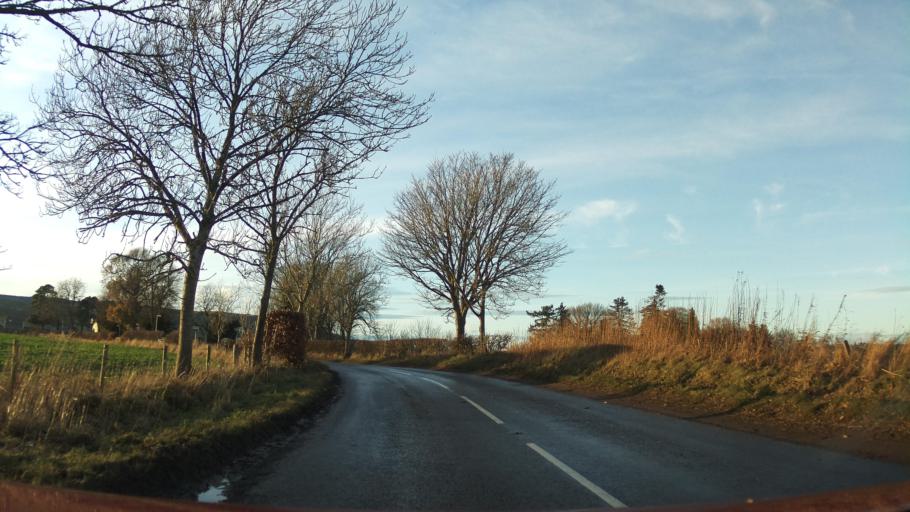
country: GB
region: Scotland
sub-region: Angus
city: Forfar
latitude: 56.5879
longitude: -2.8893
